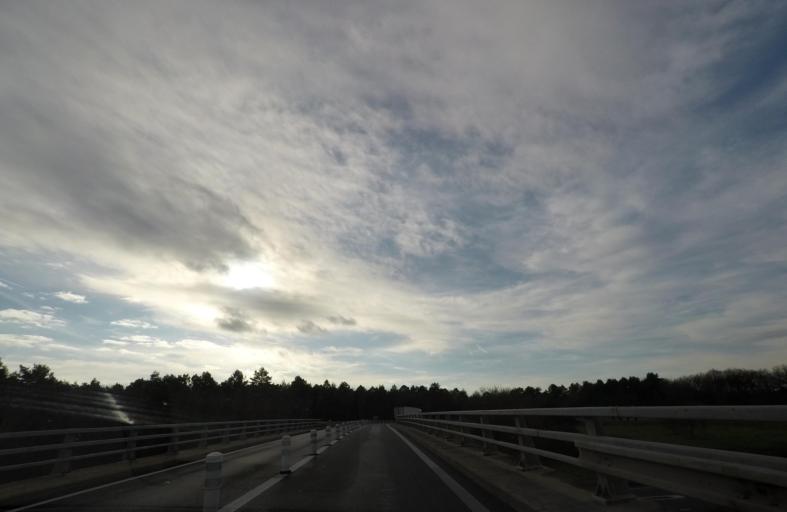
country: FR
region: Centre
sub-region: Departement du Loir-et-Cher
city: Villefranche-sur-Cher
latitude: 47.3214
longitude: 1.7684
